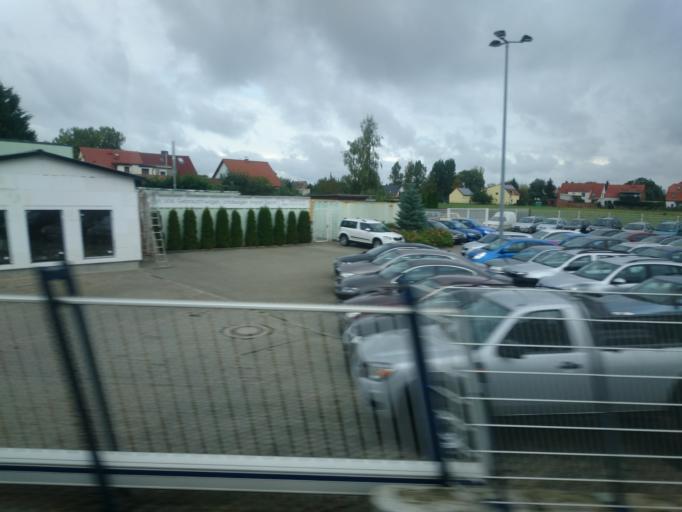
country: DE
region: Saxony-Anhalt
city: Grosskugel
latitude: 51.4152
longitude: 12.1450
